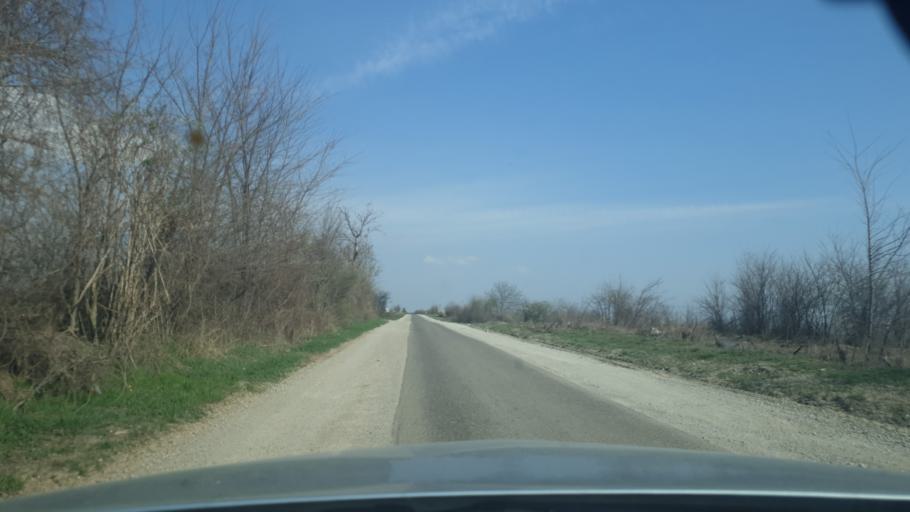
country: RS
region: Autonomna Pokrajina Vojvodina
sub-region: Sremski Okrug
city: Irig
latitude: 45.1019
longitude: 19.8962
